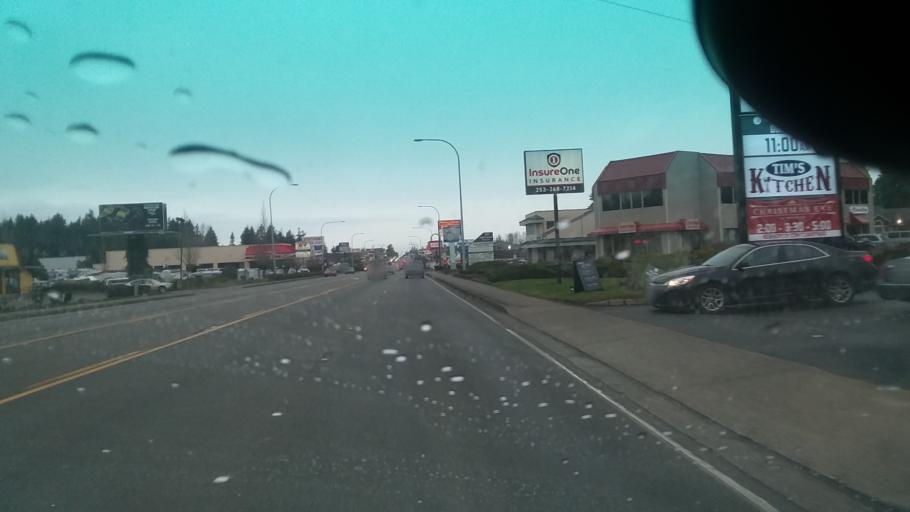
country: US
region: Washington
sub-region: Pierce County
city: South Hill
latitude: 47.1418
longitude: -122.2929
